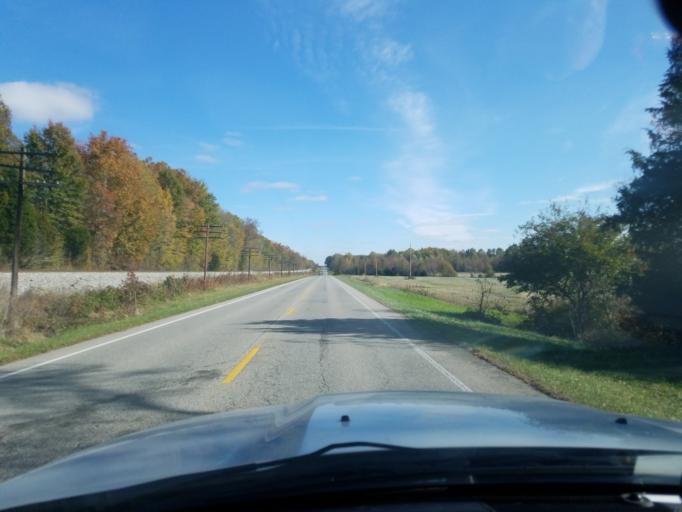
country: US
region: Indiana
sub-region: Jennings County
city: North Vernon
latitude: 39.0218
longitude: -85.5534
